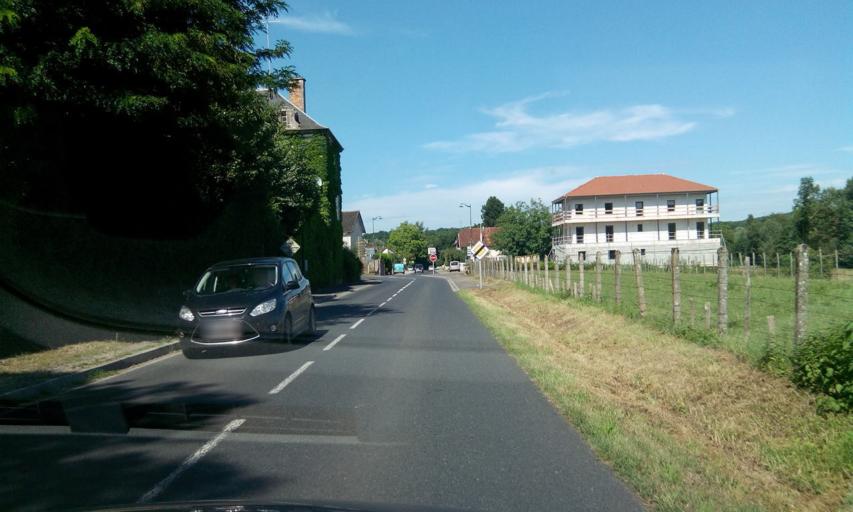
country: FR
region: Midi-Pyrenees
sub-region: Departement du Lot
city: Vayrac
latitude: 44.9522
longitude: 1.7079
